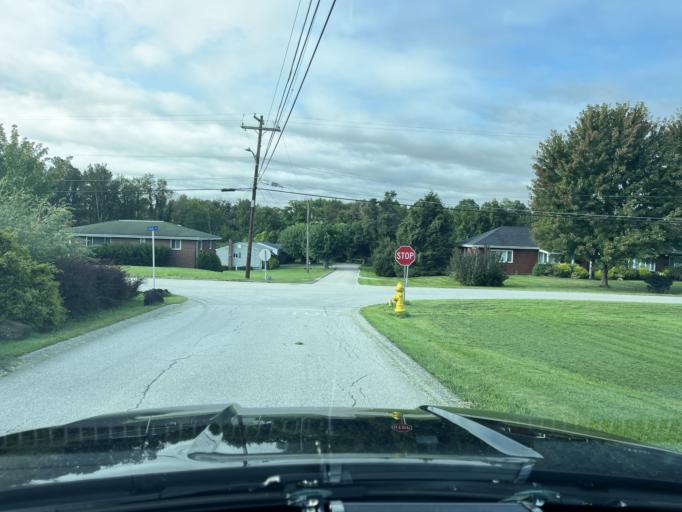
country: US
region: Pennsylvania
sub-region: Fayette County
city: Leith-Hatfield
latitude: 39.8710
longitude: -79.7403
